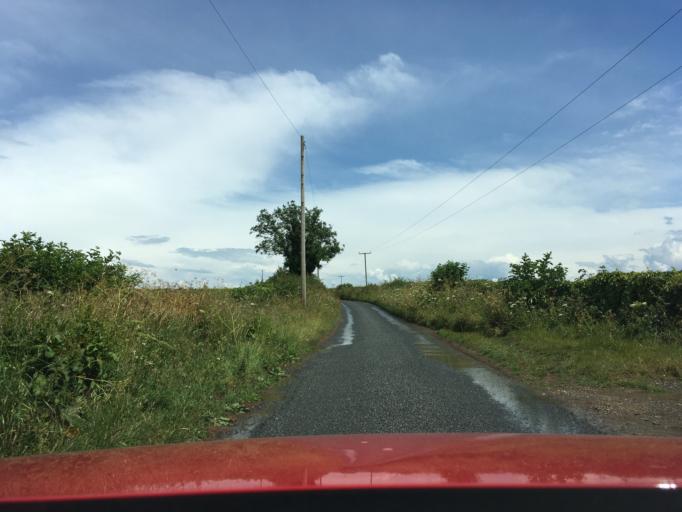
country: GB
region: England
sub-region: Wiltshire
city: Luckington
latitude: 51.6164
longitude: -2.2430
